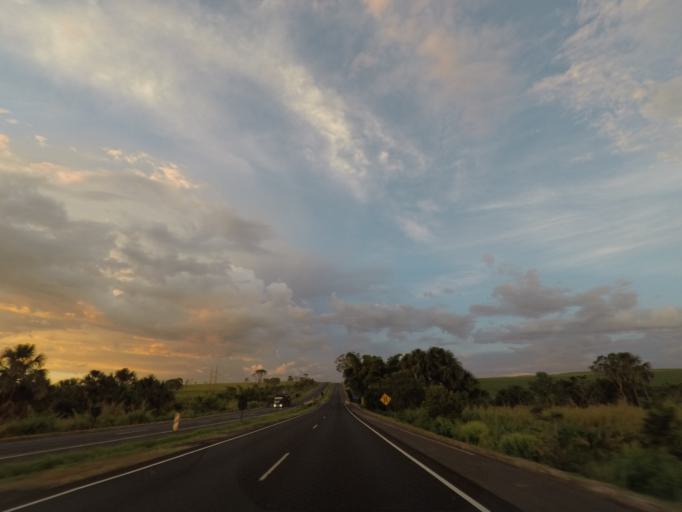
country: BR
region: Minas Gerais
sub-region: Uberaba
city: Uberaba
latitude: -19.6193
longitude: -48.0178
